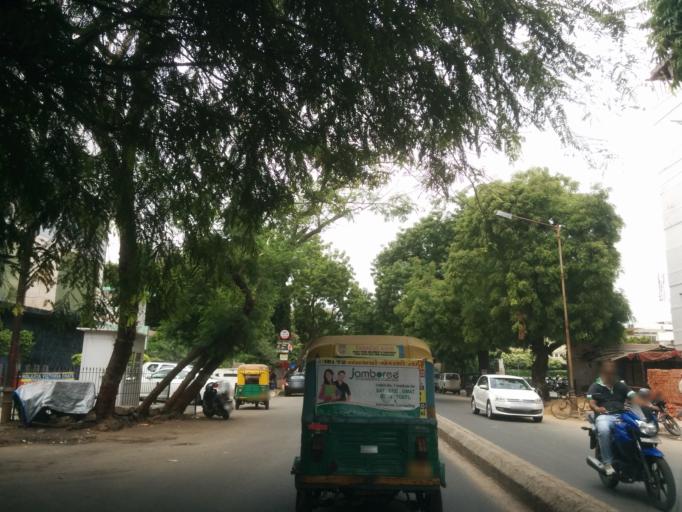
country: IN
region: Gujarat
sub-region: Ahmadabad
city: Ahmedabad
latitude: 23.0330
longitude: 72.5570
